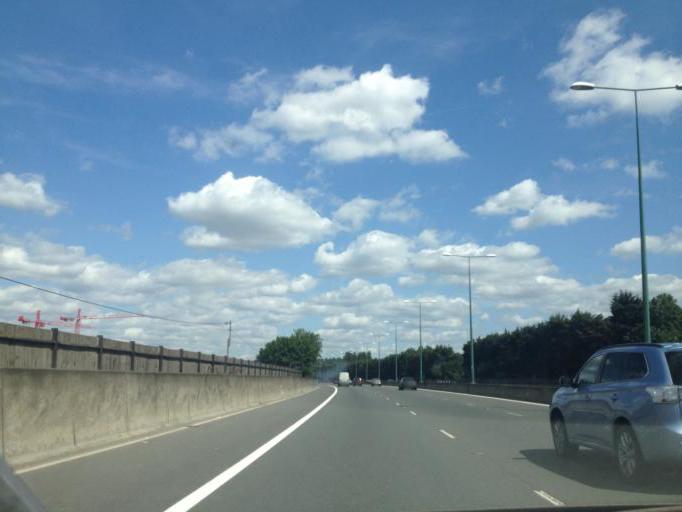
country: GB
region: England
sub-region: Greater London
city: Hendon
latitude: 51.5916
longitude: -0.2363
